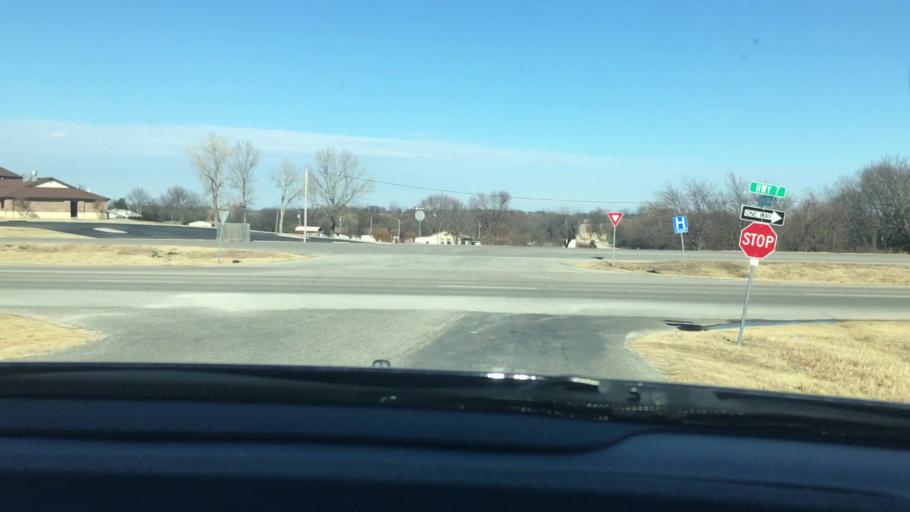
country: US
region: Oklahoma
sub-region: Murray County
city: Davis
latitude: 34.5058
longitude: -97.0552
